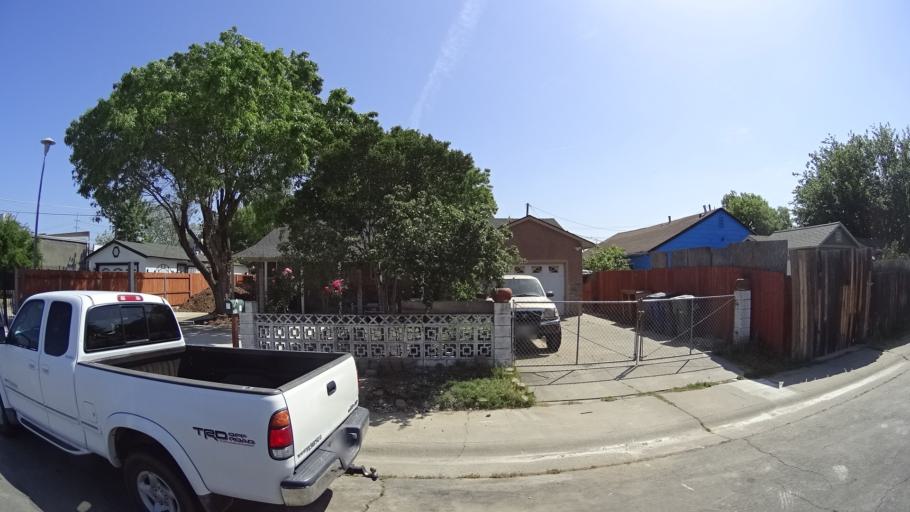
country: US
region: California
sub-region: Sacramento County
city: Parkway
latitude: 38.5072
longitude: -121.4764
